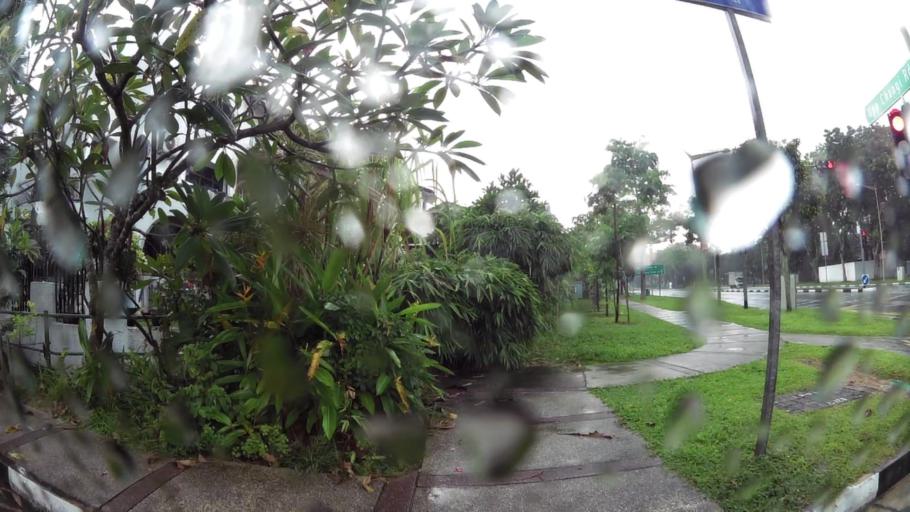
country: SG
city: Singapore
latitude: 1.3330
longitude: 103.9480
